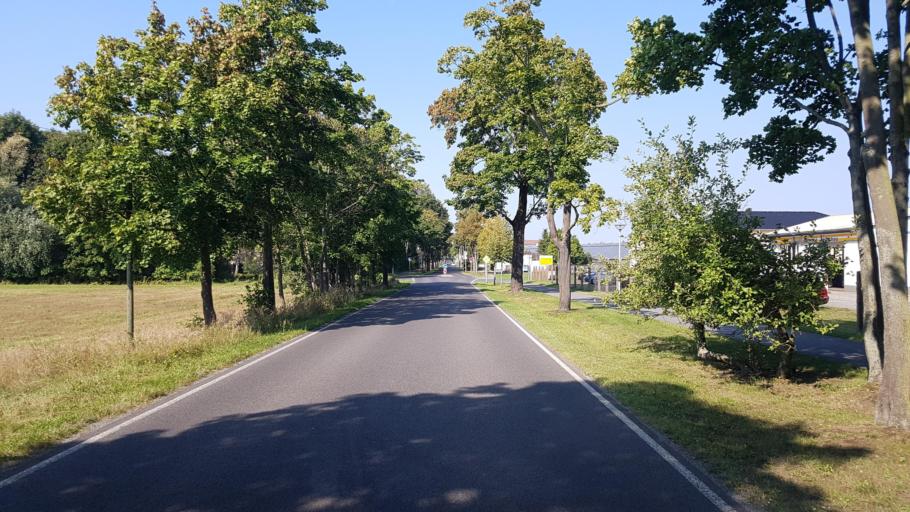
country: DE
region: Brandenburg
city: Vetschau
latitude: 51.7773
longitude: 14.0901
